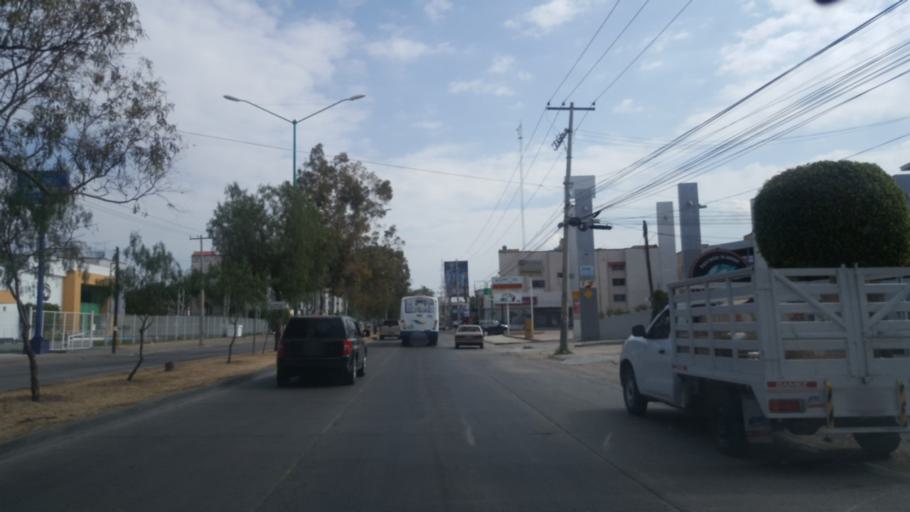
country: MX
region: Guanajuato
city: Leon
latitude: 21.1041
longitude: -101.6445
